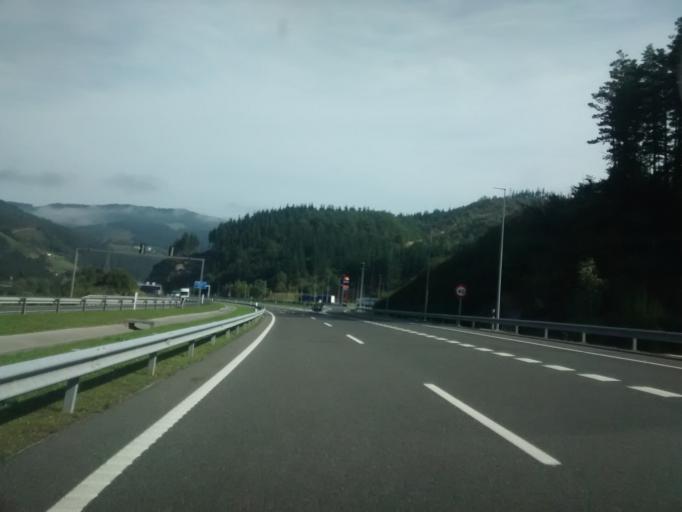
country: ES
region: Basque Country
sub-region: Provincia de Guipuzcoa
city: Arrasate / Mondragon
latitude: 43.0620
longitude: -2.4781
